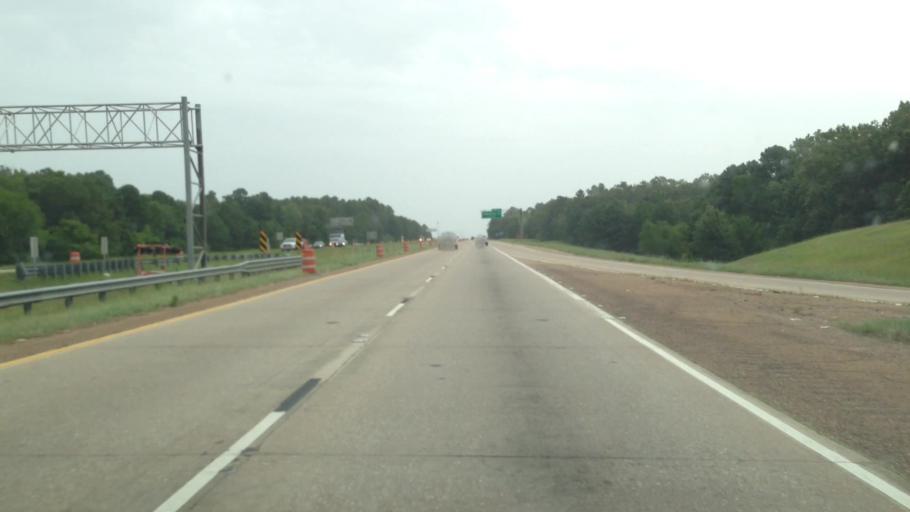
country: US
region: Louisiana
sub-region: Caddo Parish
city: Shreveport
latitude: 32.4753
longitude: -93.8356
